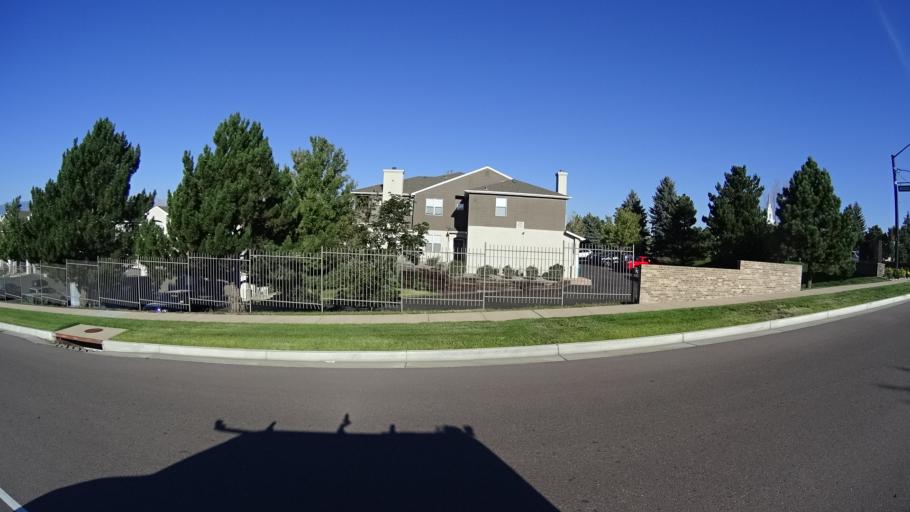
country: US
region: Colorado
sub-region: El Paso County
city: Black Forest
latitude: 38.9564
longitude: -104.7698
